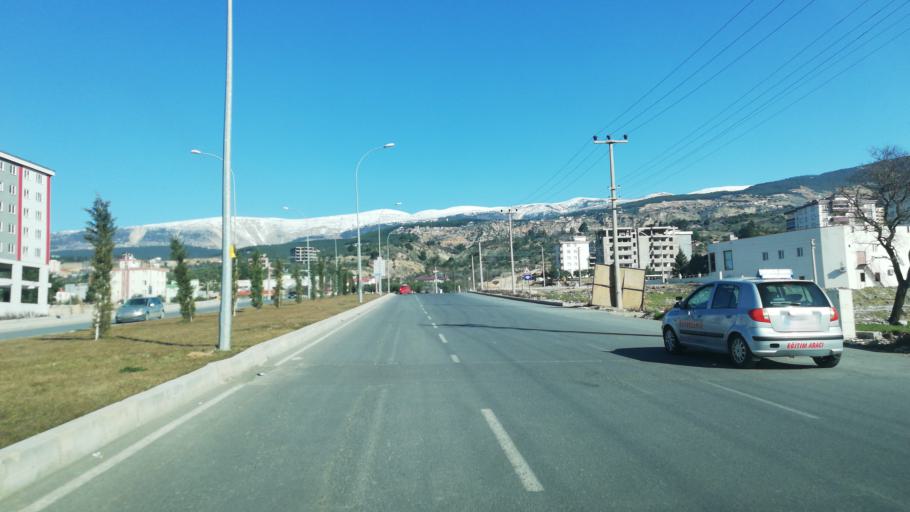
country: TR
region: Kahramanmaras
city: Kahramanmaras
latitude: 37.5809
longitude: 36.9746
